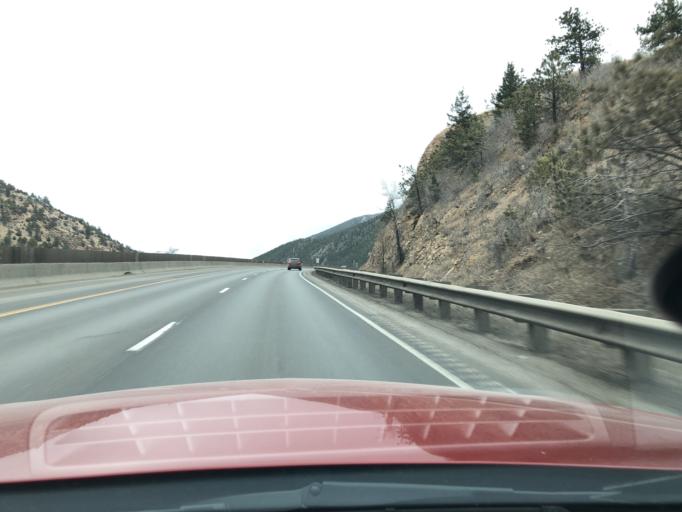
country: US
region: Colorado
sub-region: Clear Creek County
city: Idaho Springs
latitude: 39.7413
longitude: -105.5117
